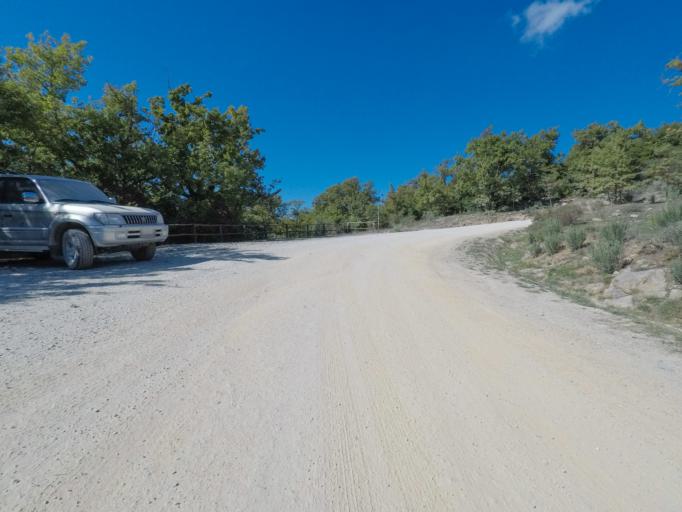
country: IT
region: Tuscany
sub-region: Provincia di Siena
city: Castellina in Chianti
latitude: 43.4358
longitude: 11.3013
